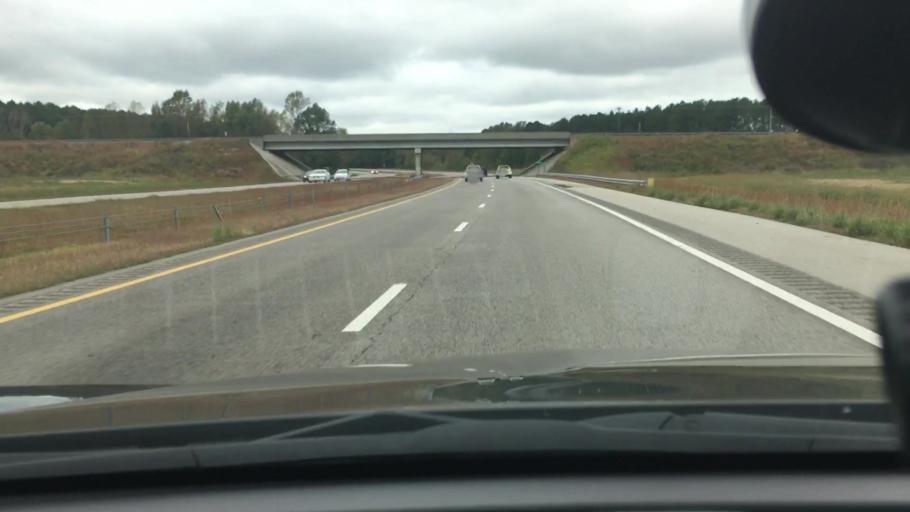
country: US
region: North Carolina
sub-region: Wilson County
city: Wilson
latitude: 35.6671
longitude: -77.7627
